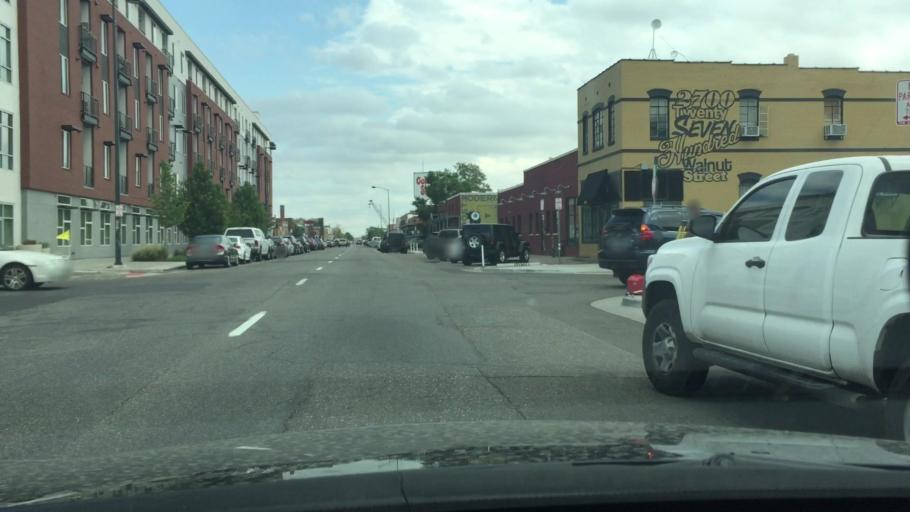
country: US
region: Colorado
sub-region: Denver County
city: Denver
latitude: 39.7600
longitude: -104.9852
